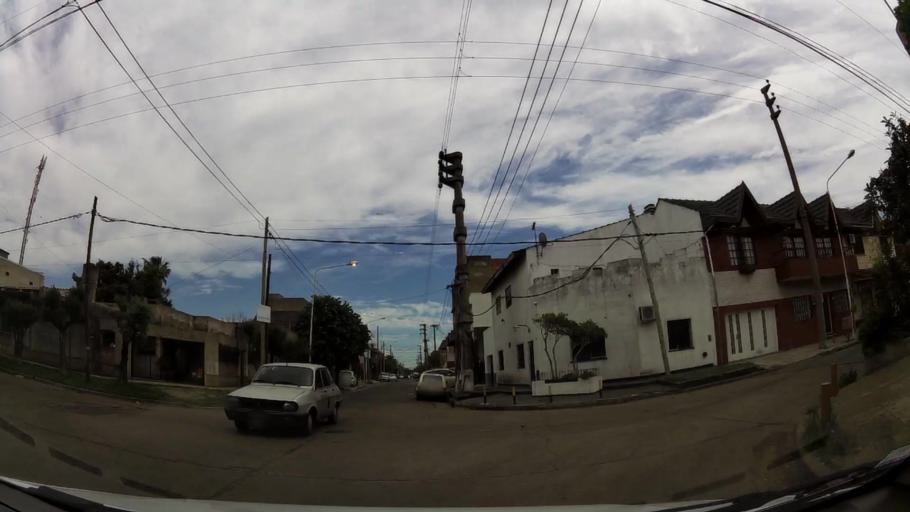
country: AR
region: Buenos Aires
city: San Justo
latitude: -34.6757
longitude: -58.5374
